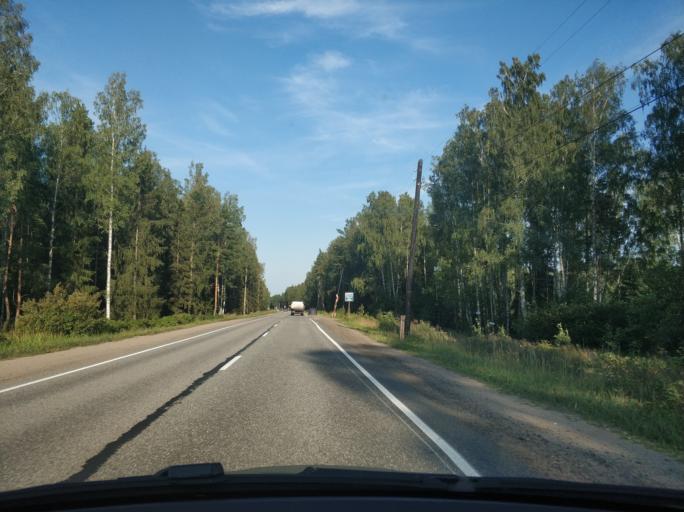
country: RU
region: Leningrad
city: Borisova Griva
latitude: 60.0919
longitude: 30.9946
